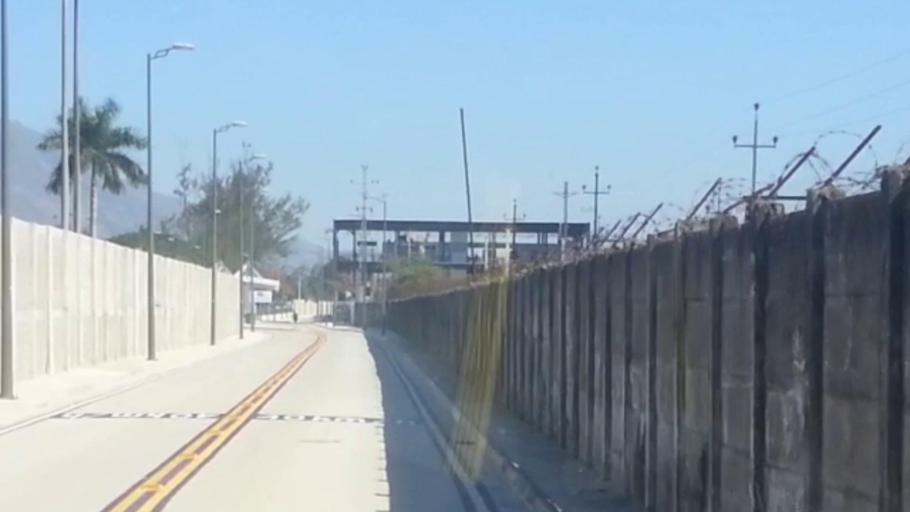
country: BR
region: Rio de Janeiro
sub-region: Nilopolis
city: Nilopolis
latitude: -22.8611
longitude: -43.3986
